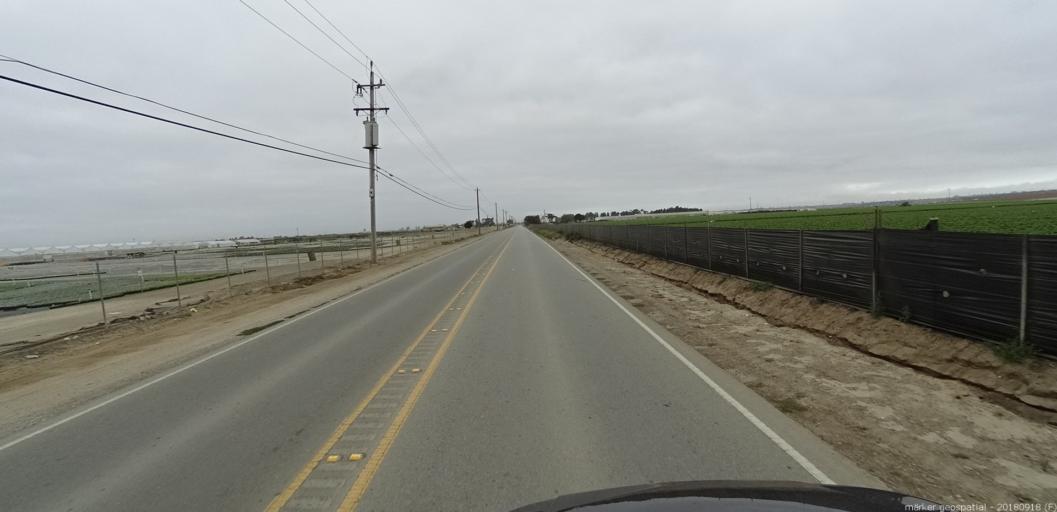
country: US
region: California
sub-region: Monterey County
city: Prunedale
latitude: 36.7404
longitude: -121.6777
